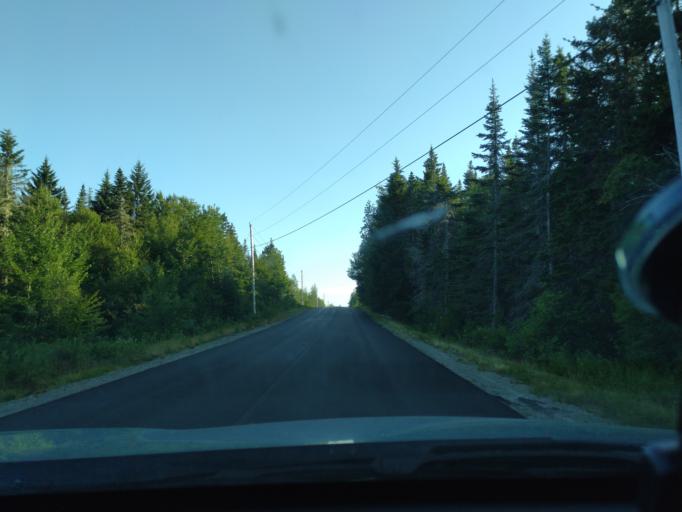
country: US
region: Maine
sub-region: Washington County
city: Machiasport
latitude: 44.6924
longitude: -67.1649
